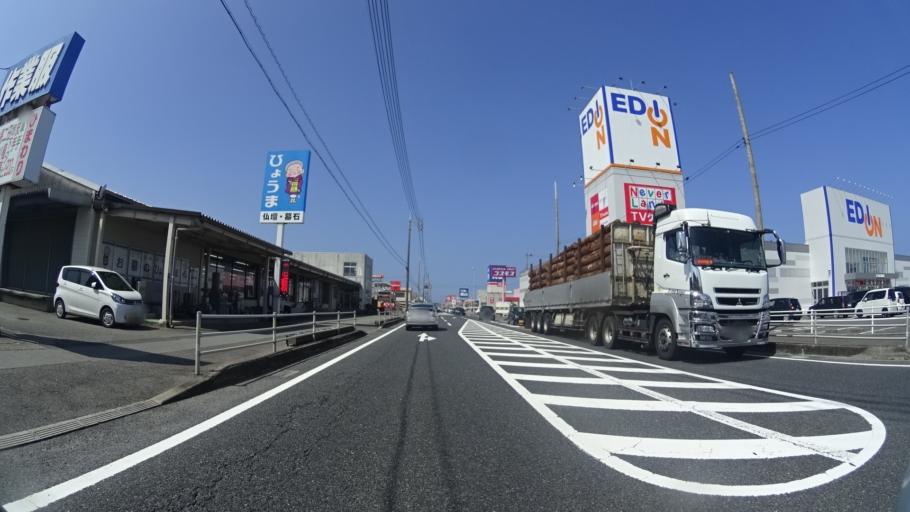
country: JP
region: Shimane
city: Masuda
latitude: 34.6892
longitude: 131.8214
